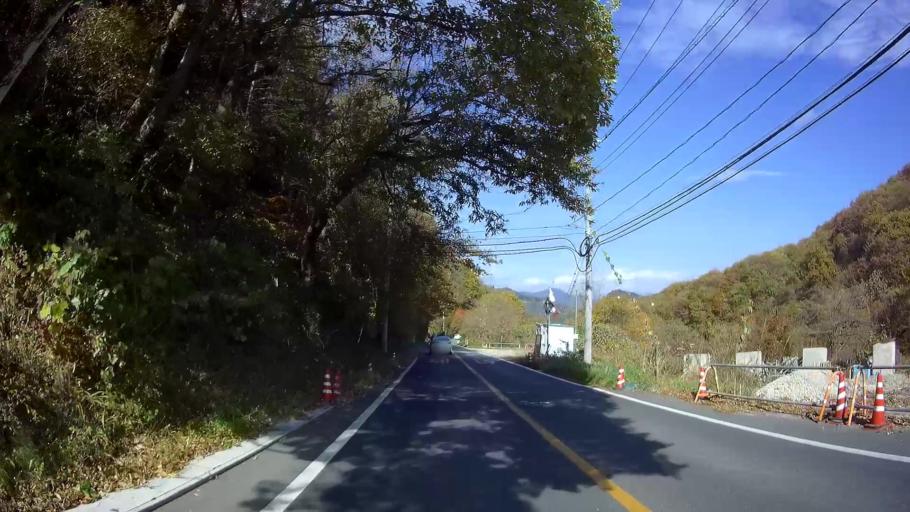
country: JP
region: Gunma
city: Nakanojomachi
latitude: 36.4958
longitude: 138.7770
